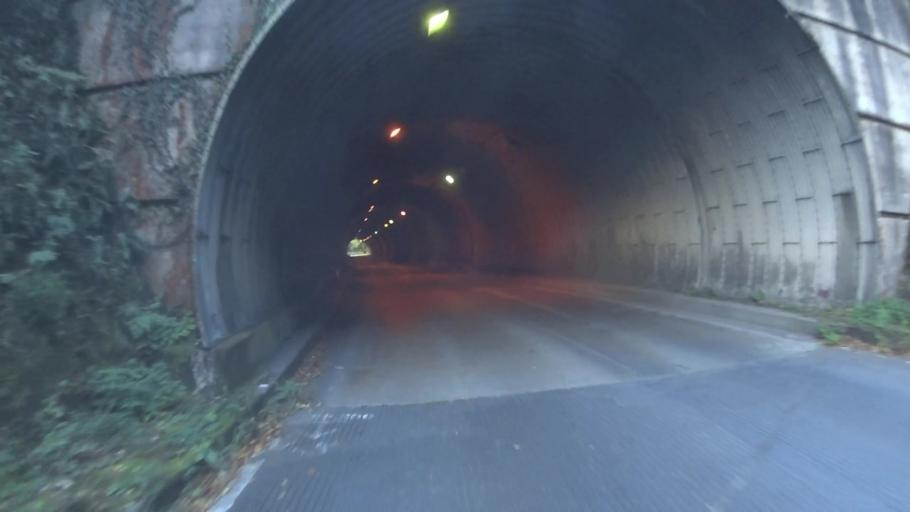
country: JP
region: Kyoto
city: Maizuru
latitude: 35.4638
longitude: 135.2503
